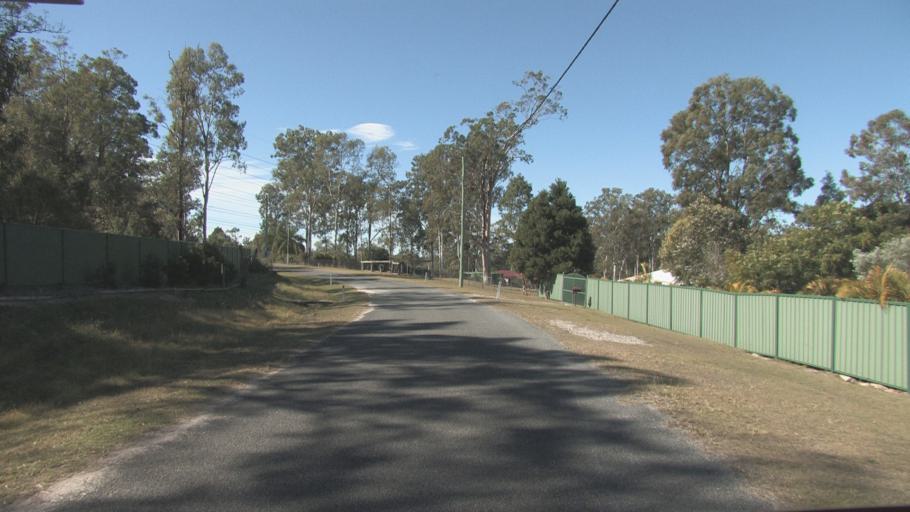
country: AU
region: Queensland
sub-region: Ipswich
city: Springfield Lakes
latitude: -27.7241
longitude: 152.9375
